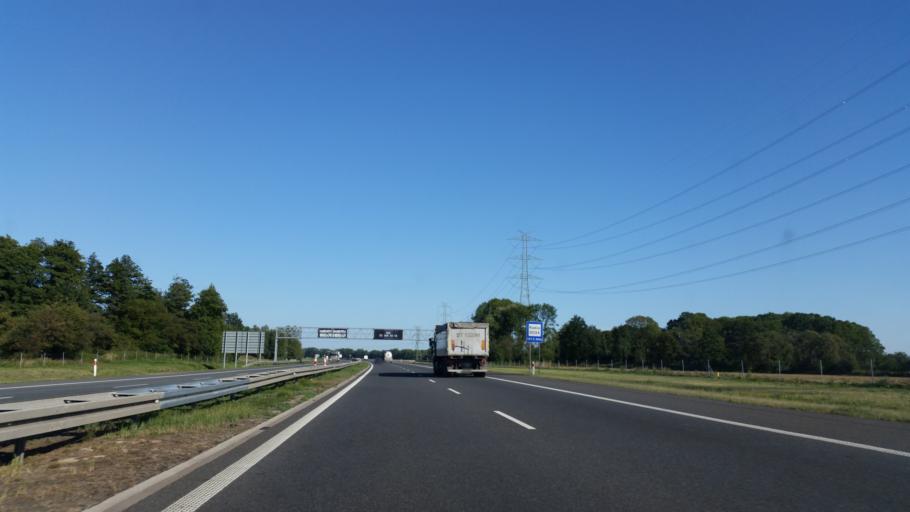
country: PL
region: Opole Voivodeship
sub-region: Powiat brzeski
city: Grodkow
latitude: 50.7764
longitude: 17.3601
